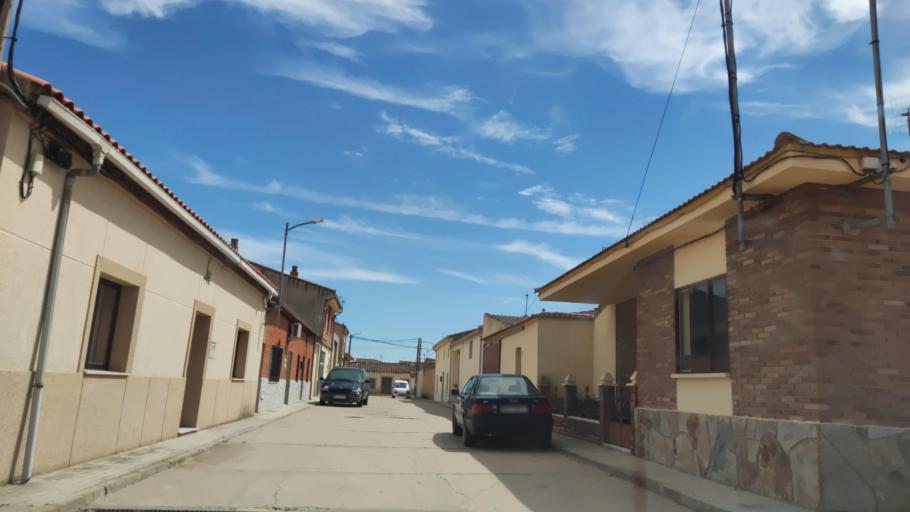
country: ES
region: Castille and Leon
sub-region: Provincia de Zamora
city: Villalazan
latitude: 41.4953
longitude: -5.5883
